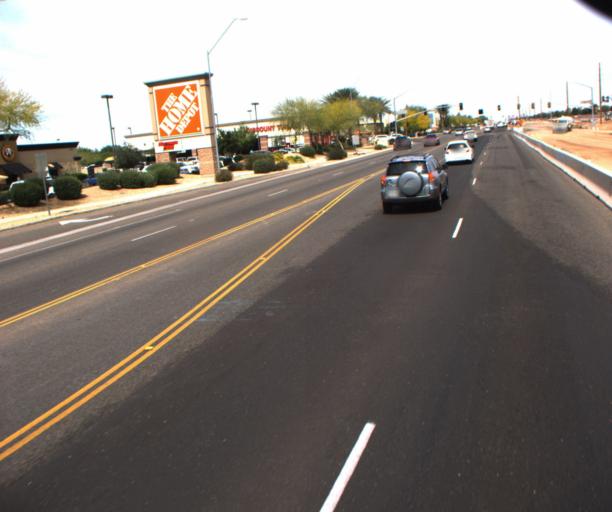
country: US
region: Arizona
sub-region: Maricopa County
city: Surprise
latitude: 33.6414
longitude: -112.3539
